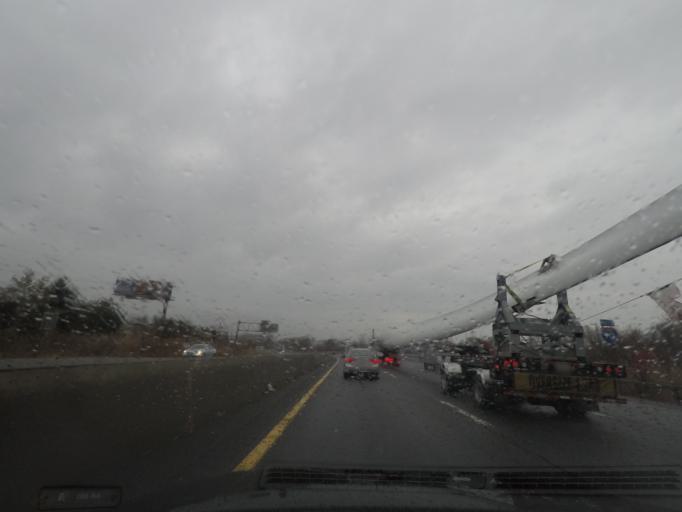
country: US
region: New York
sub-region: Albany County
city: West Albany
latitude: 42.6852
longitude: -73.7902
